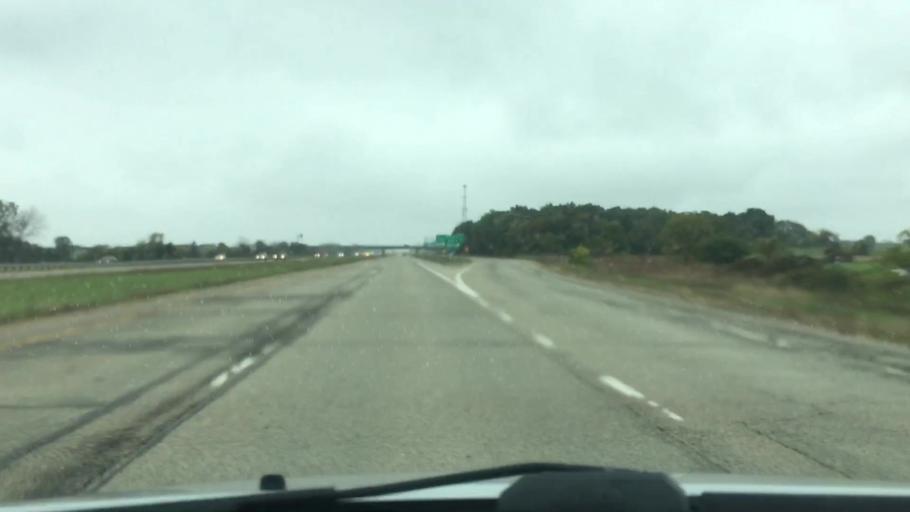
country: US
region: Wisconsin
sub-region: Walworth County
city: Elkhorn
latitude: 42.6797
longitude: -88.5258
